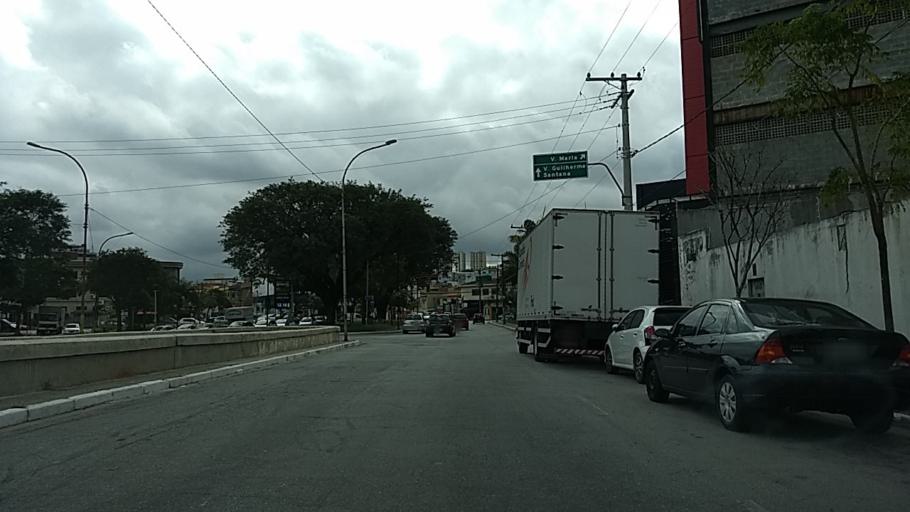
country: BR
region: Sao Paulo
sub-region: Sao Paulo
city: Sao Paulo
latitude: -23.5111
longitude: -46.5949
